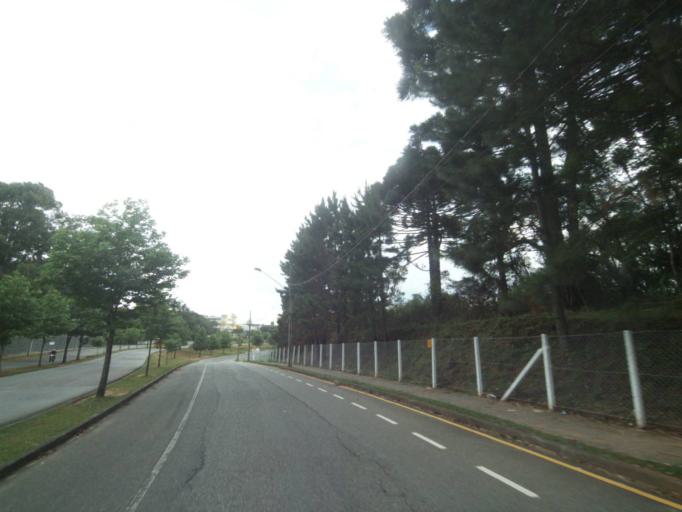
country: BR
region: Parana
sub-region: Curitiba
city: Curitiba
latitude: -25.4472
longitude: -49.3544
